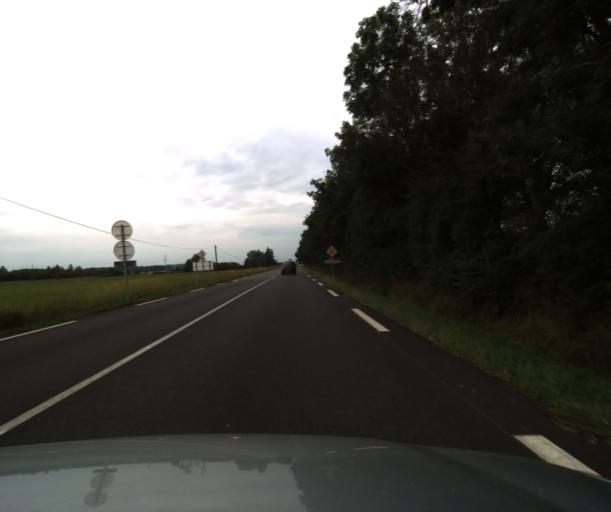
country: FR
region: Midi-Pyrenees
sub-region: Departement des Hautes-Pyrenees
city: Rabastens-de-Bigorre
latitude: 43.3789
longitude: 0.1476
